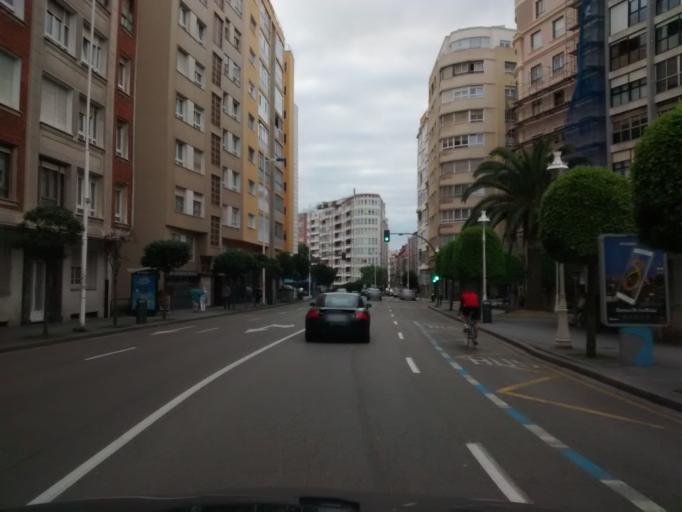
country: ES
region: Cantabria
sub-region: Provincia de Cantabria
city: Santander
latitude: 43.4636
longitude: -3.7879
